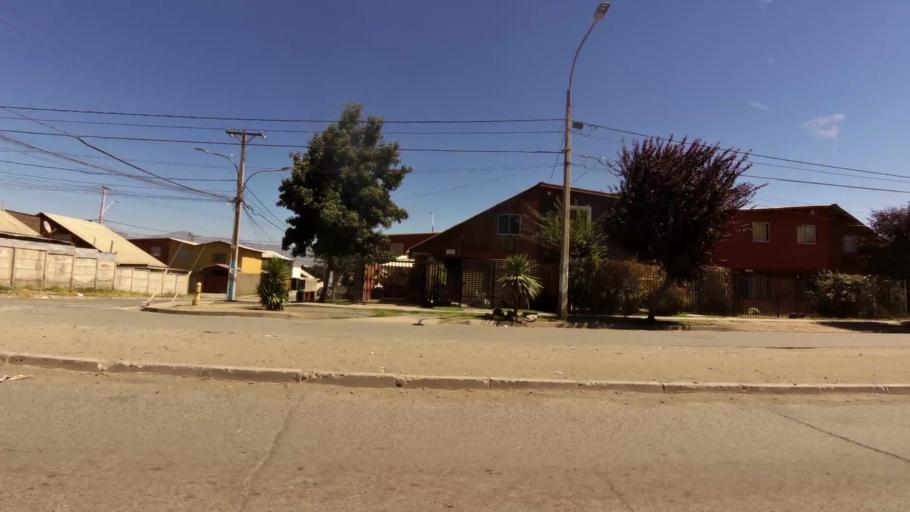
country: CL
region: O'Higgins
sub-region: Provincia de Cachapoal
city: Rancagua
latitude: -34.1513
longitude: -70.7244
